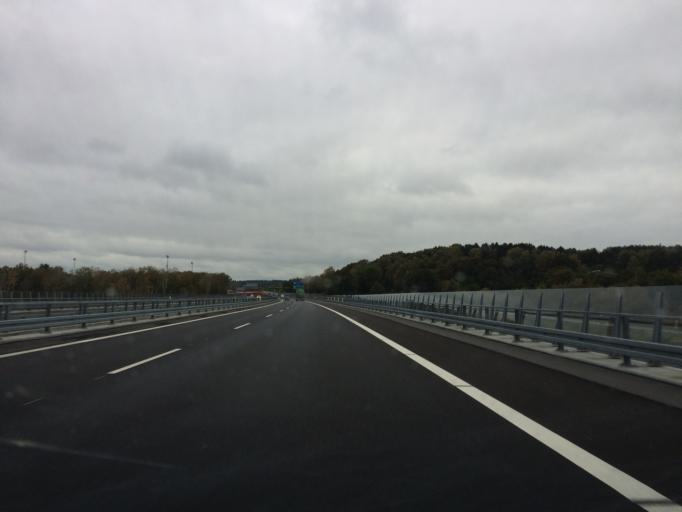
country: DK
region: Central Jutland
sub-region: Silkeborg Kommune
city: Svejbaek
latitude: 56.1735
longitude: 9.5989
